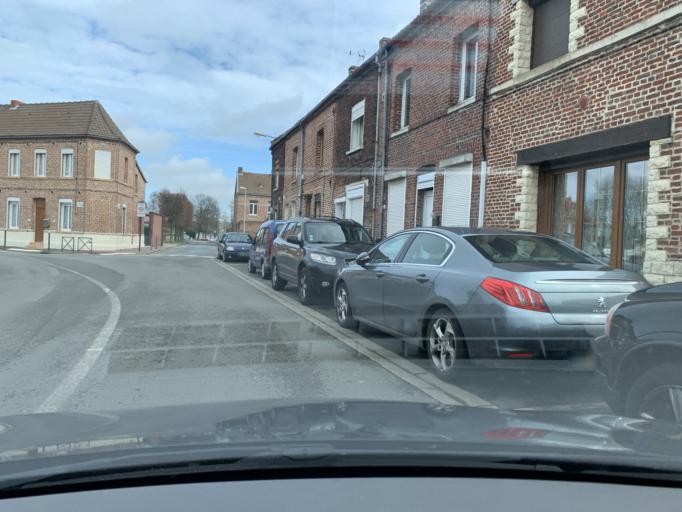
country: FR
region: Nord-Pas-de-Calais
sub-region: Departement du Nord
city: Waziers
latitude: 50.3936
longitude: 3.0880
